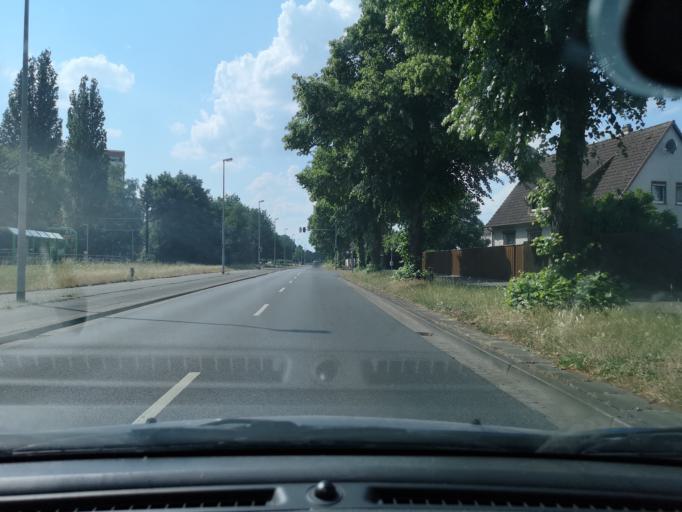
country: DE
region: Lower Saxony
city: Langenhagen
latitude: 52.4196
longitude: 9.7602
